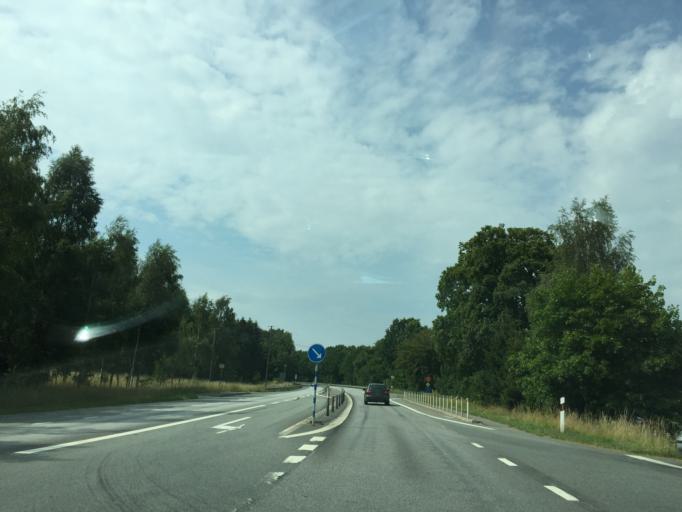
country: SE
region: Skane
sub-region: Sjobo Kommun
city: Sjoebo
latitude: 55.6124
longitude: 13.7752
